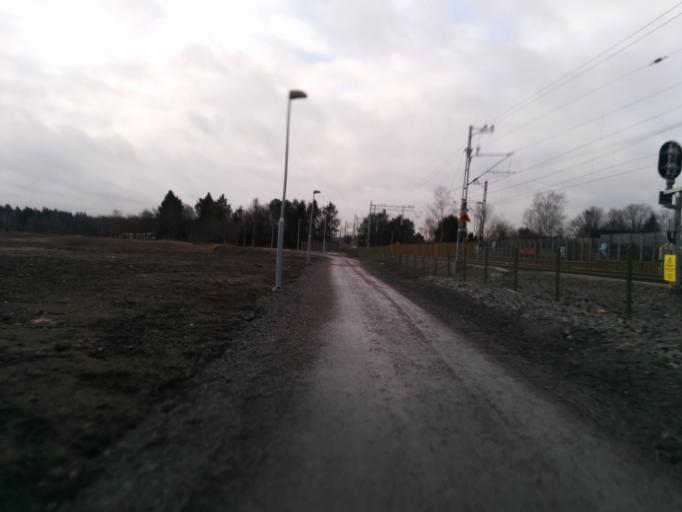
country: SE
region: Stockholm
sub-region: Taby Kommun
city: Taby
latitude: 59.4891
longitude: 18.0628
